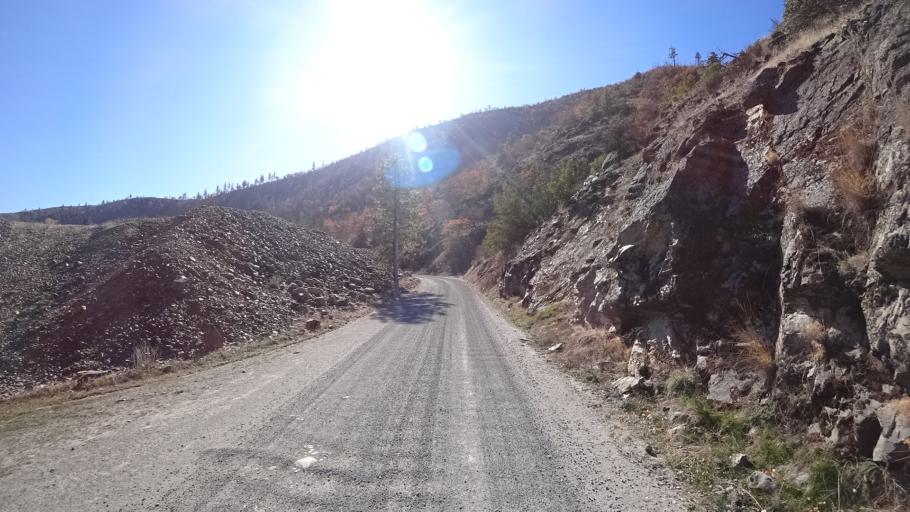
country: US
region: California
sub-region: Siskiyou County
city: Yreka
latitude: 41.8437
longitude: -122.6846
